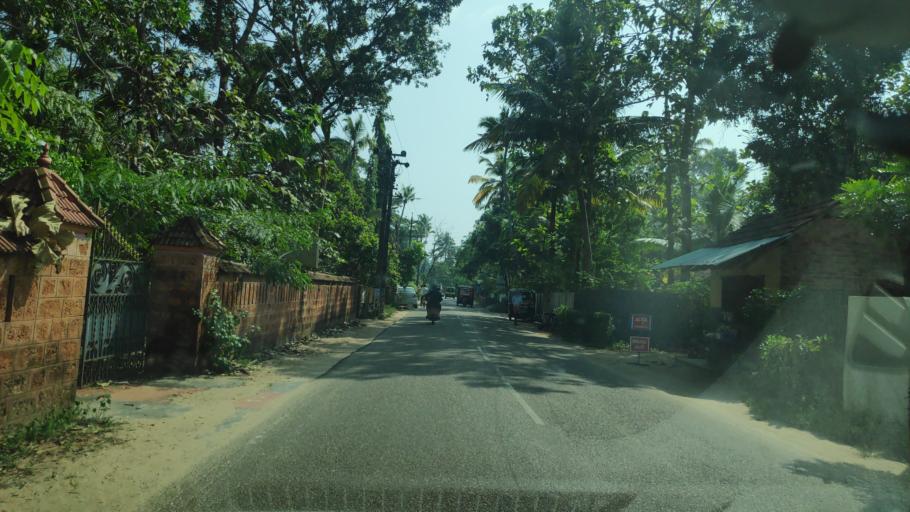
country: IN
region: Kerala
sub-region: Alappuzha
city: Vayalar
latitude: 9.6523
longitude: 76.2996
